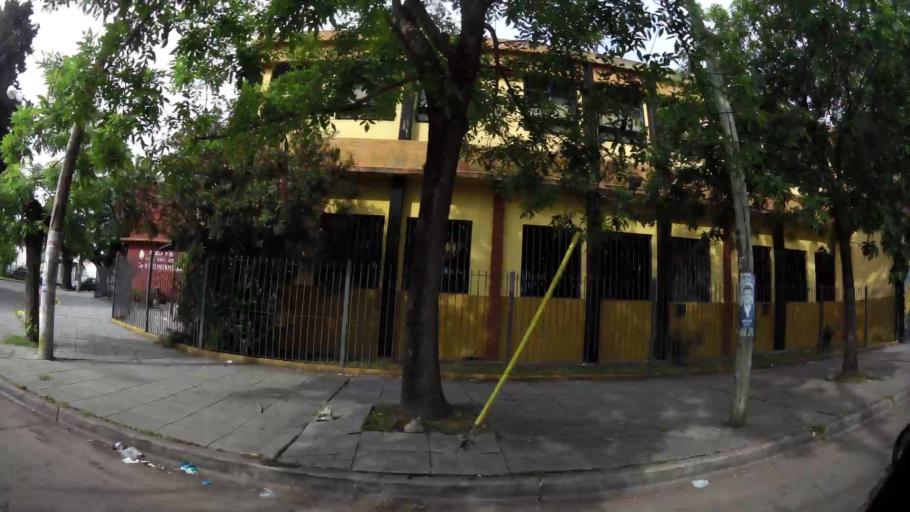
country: AR
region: Buenos Aires
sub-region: Partido de Quilmes
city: Quilmes
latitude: -34.7548
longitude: -58.2785
